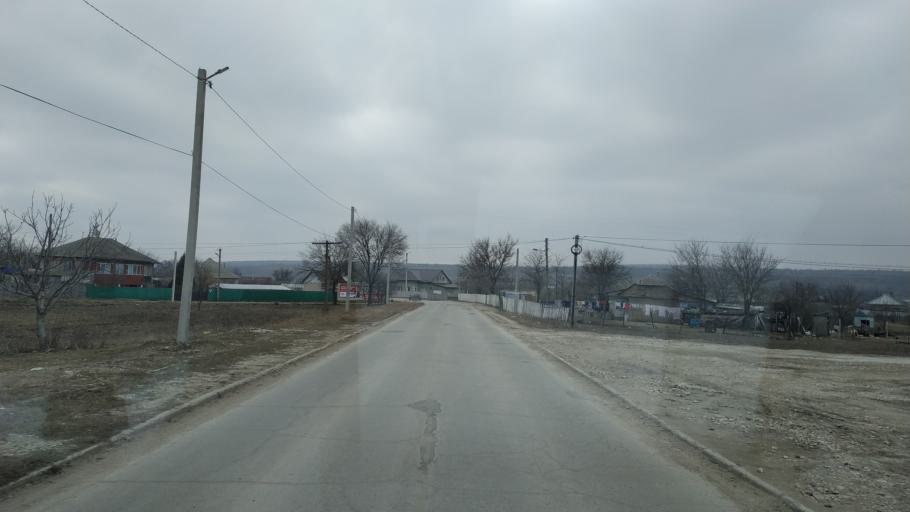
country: MD
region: Hincesti
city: Hincesti
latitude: 46.8770
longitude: 28.4057
